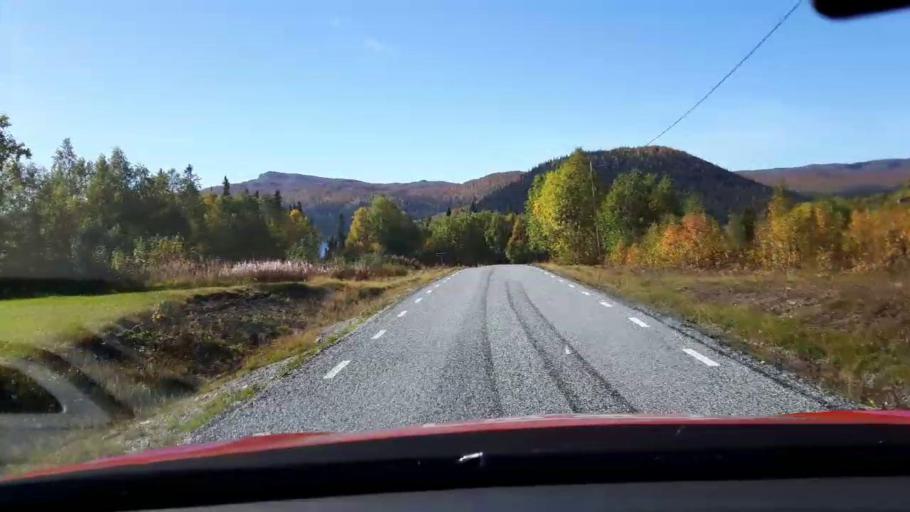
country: NO
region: Nord-Trondelag
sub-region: Royrvik
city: Royrvik
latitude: 64.8749
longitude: 14.2412
